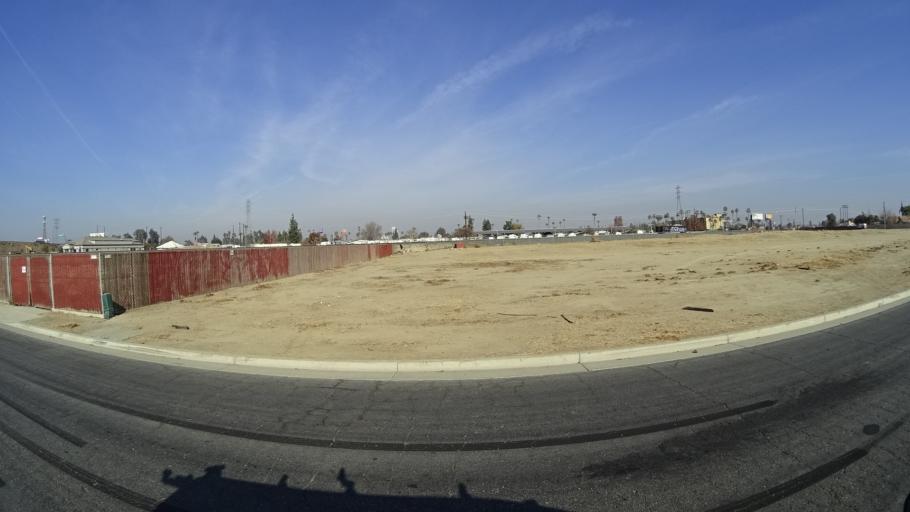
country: US
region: California
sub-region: Kern County
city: Greenfield
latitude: 35.3121
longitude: -119.0319
